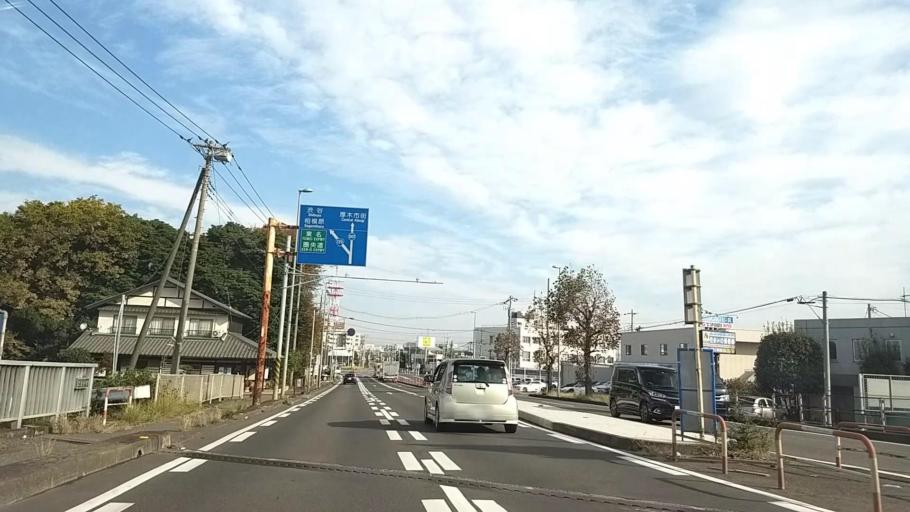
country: JP
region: Kanagawa
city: Atsugi
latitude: 35.4128
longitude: 139.3625
